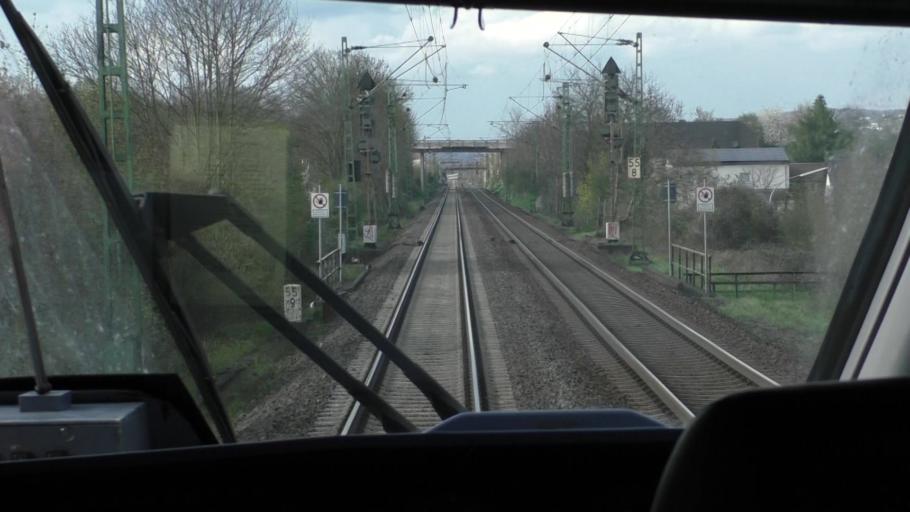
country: DE
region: Rheinland-Pfalz
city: Sinzig
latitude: 50.5532
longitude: 7.2535
